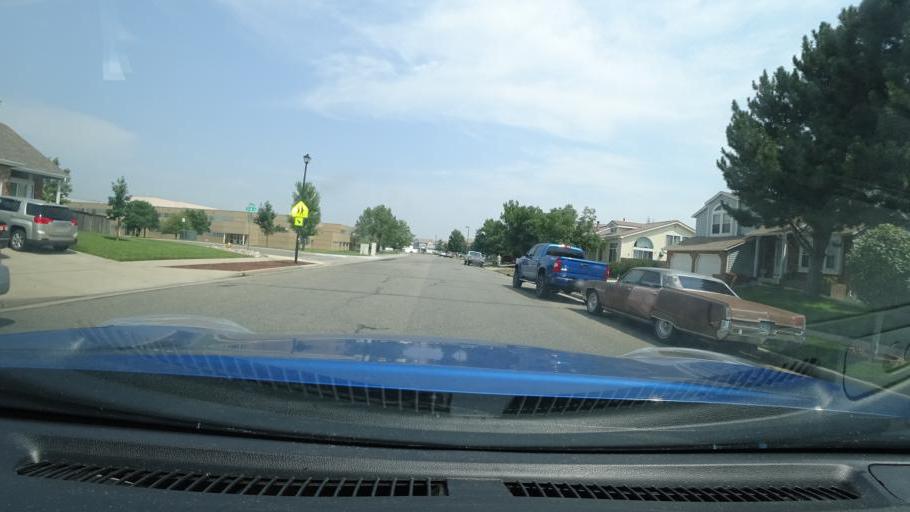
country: US
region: Colorado
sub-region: Adams County
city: Aurora
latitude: 39.7797
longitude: -104.7590
